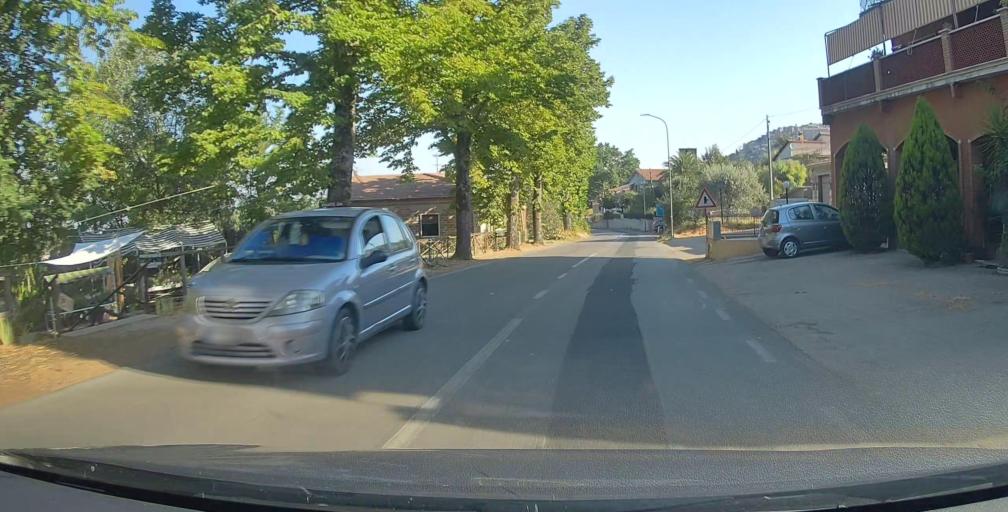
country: IT
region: Umbria
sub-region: Provincia di Terni
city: Calvi dell'Umbria
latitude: 42.3920
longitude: 12.5651
